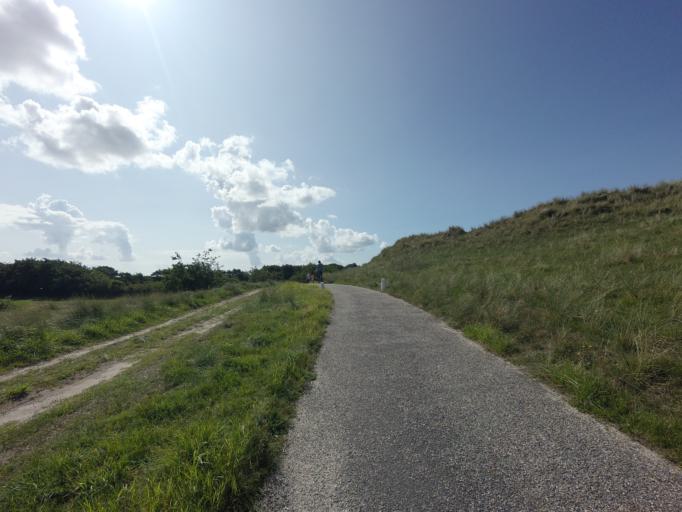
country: NL
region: Friesland
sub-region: Gemeente Terschelling
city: West-Terschelling
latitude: 53.4071
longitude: 5.3903
